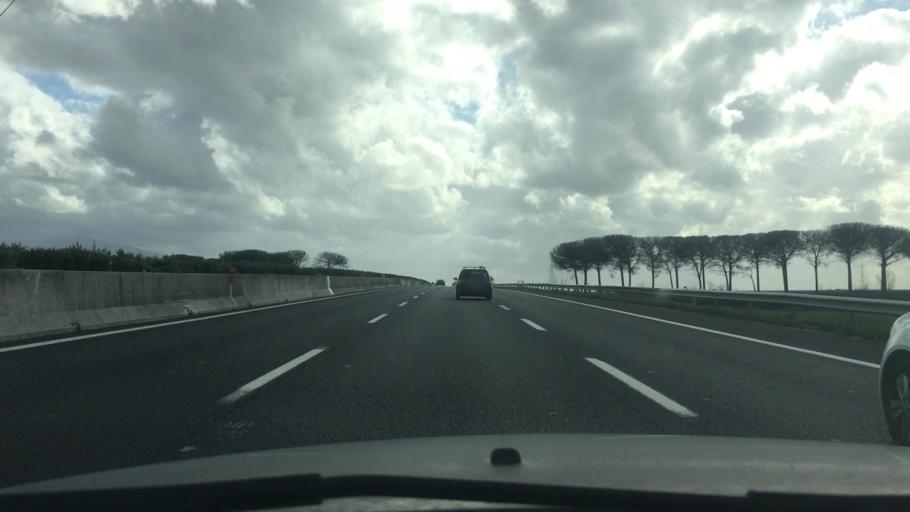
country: IT
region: Campania
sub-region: Provincia di Napoli
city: Pascarola
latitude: 40.9887
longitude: 14.3249
